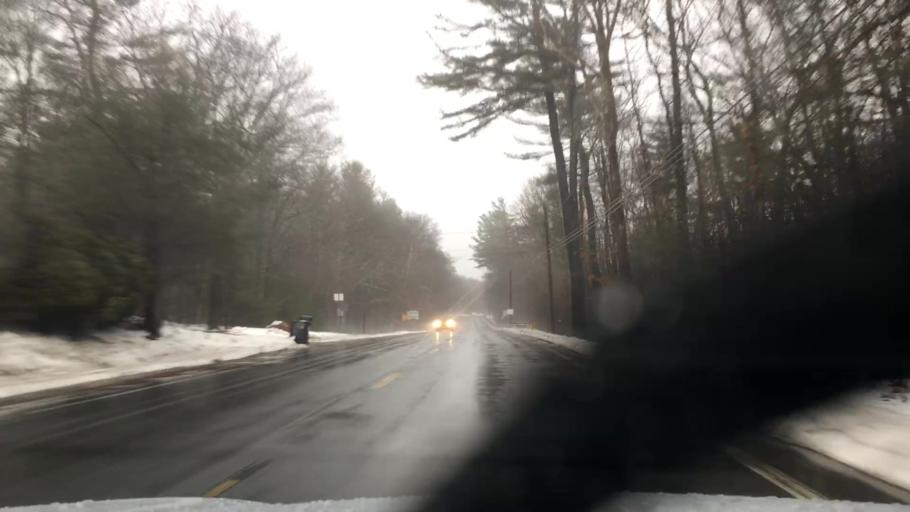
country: US
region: Massachusetts
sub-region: Hampshire County
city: Pelham
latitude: 42.3359
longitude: -72.4022
